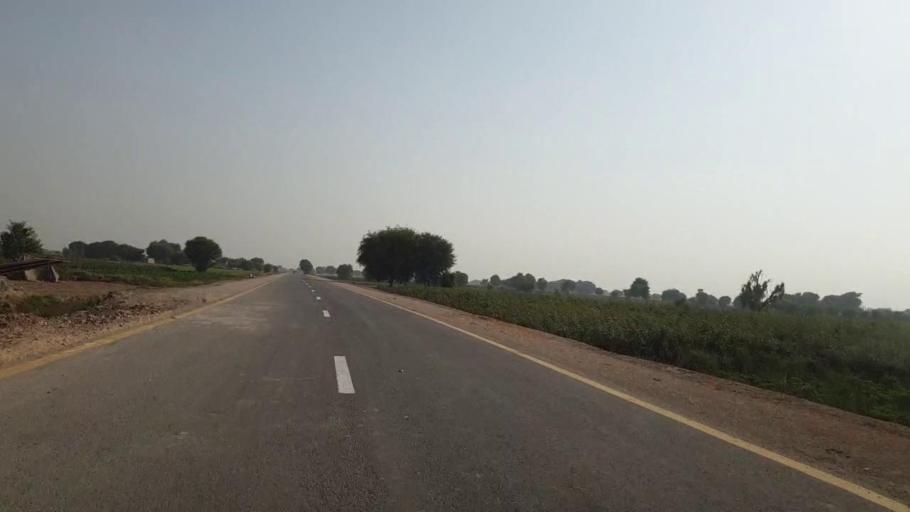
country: PK
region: Sindh
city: Bhan
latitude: 26.5312
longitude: 67.7888
